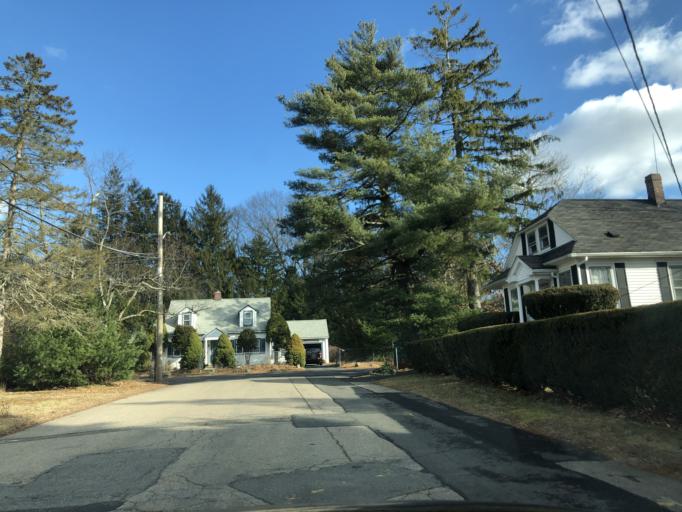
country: US
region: Massachusetts
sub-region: Plymouth County
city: Brockton
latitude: 42.1052
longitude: -71.0096
